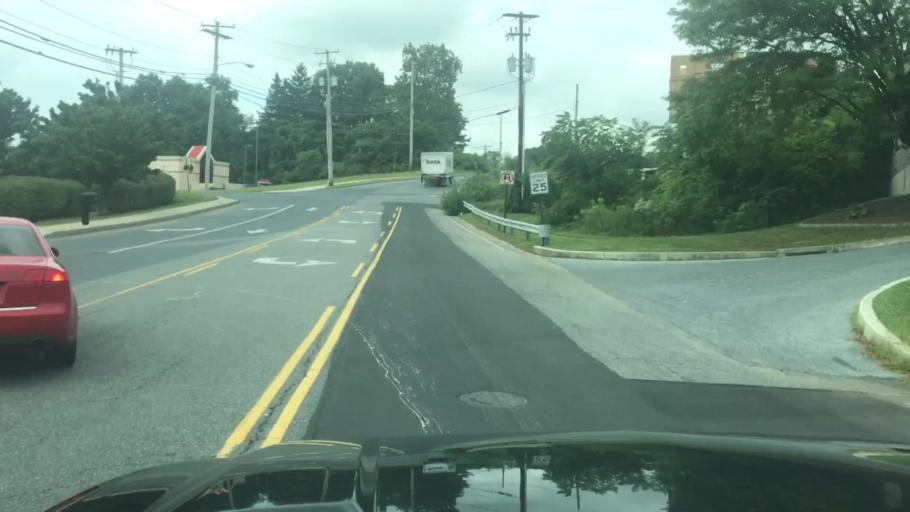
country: US
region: Pennsylvania
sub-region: Dauphin County
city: Progress
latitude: 40.3084
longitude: -76.8506
